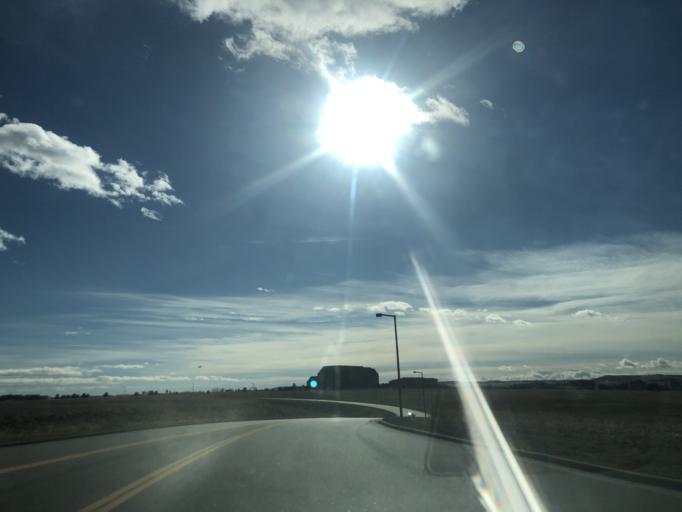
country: US
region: Colorado
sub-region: Douglas County
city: Meridian
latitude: 39.5570
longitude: -104.8570
